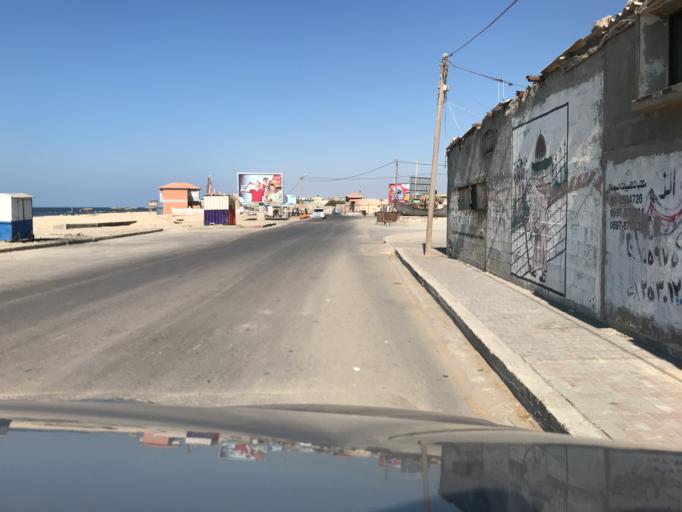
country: PS
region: Gaza Strip
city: Dayr al Balah
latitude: 31.4291
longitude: 34.3424
